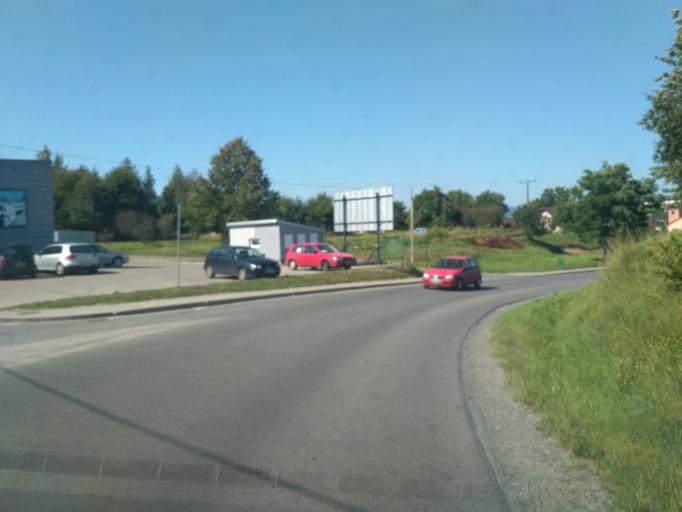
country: PL
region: Subcarpathian Voivodeship
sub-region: Krosno
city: Krosno
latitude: 49.6582
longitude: 21.7504
